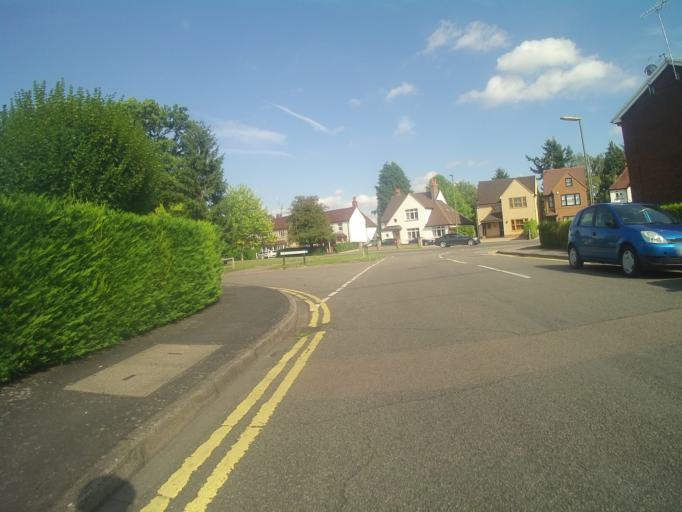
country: GB
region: England
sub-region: Surrey
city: Woking
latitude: 51.3146
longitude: -0.5750
